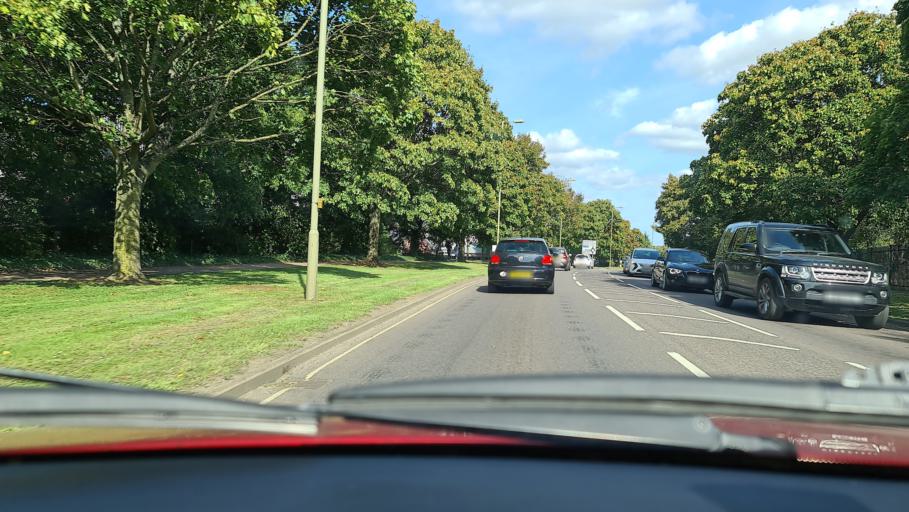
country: GB
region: England
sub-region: Oxfordshire
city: Banbury
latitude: 52.0721
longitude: -1.3429
